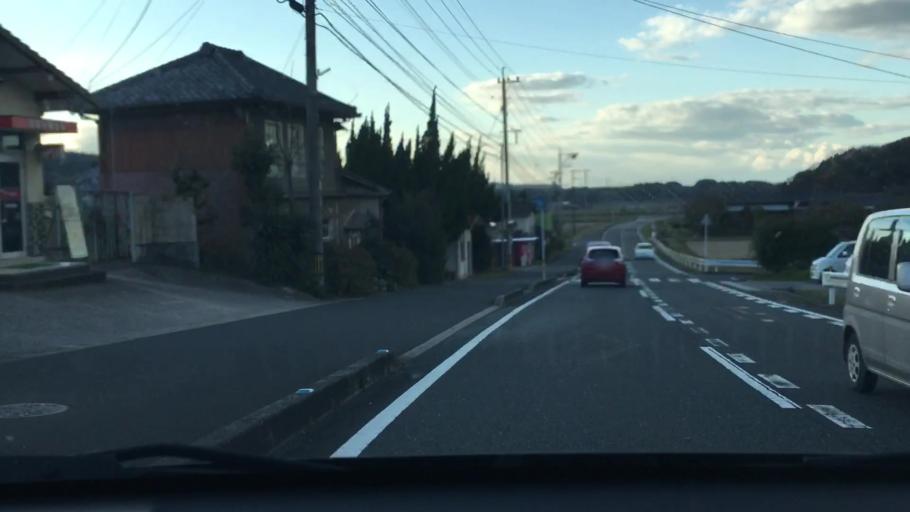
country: JP
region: Oita
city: Bungo-Takada-shi
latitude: 33.5038
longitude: 131.3666
